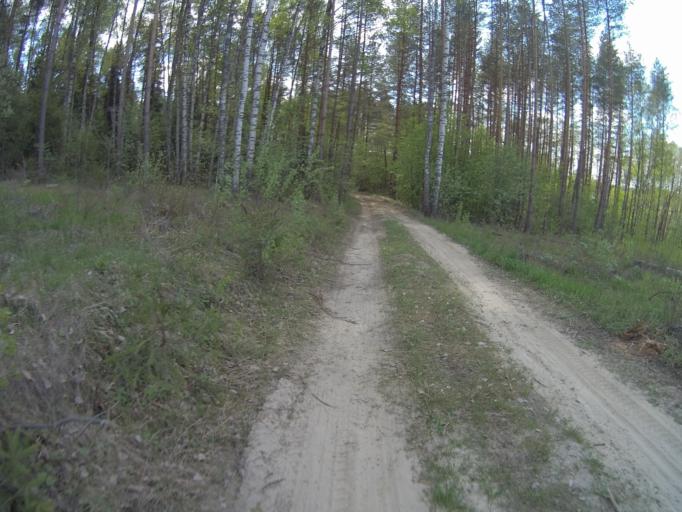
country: RU
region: Vladimir
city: Raduzhnyy
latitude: 56.0141
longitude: 40.2721
